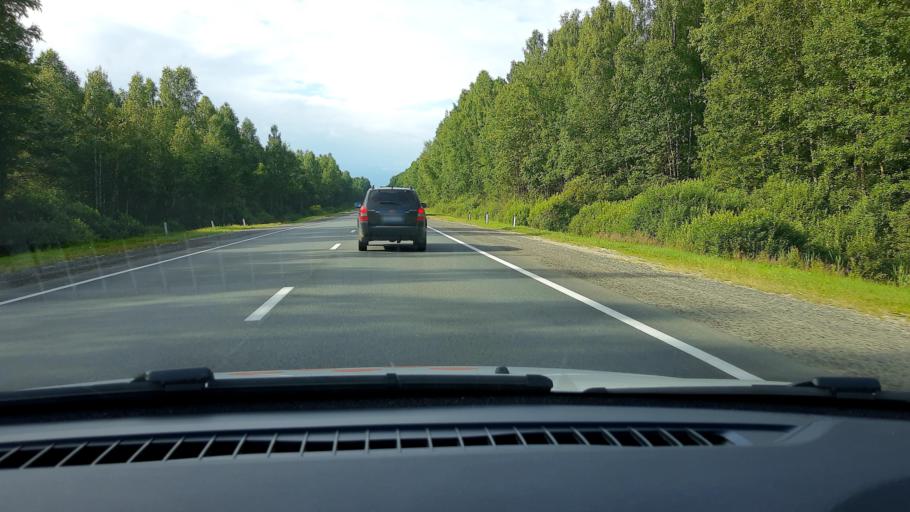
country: RU
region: Nizjnij Novgorod
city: Arzamas
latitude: 55.4747
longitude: 43.8824
